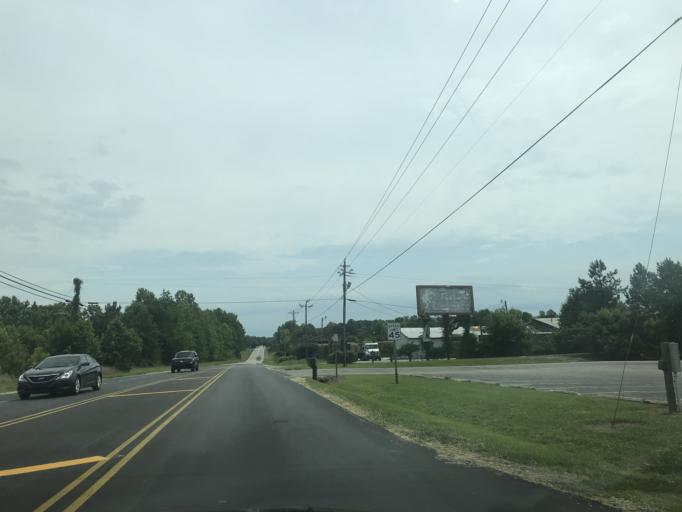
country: US
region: North Carolina
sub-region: Vance County
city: South Henderson
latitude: 36.2947
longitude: -78.4053
